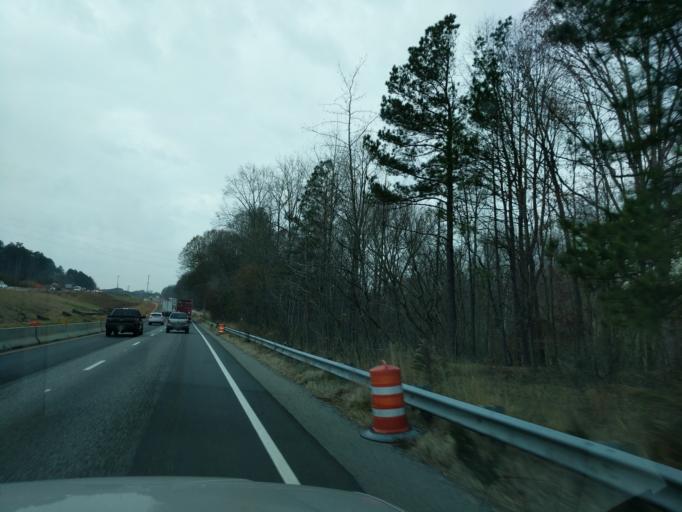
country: US
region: Georgia
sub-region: Gwinnett County
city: Suwanee
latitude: 34.0526
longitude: -84.0156
